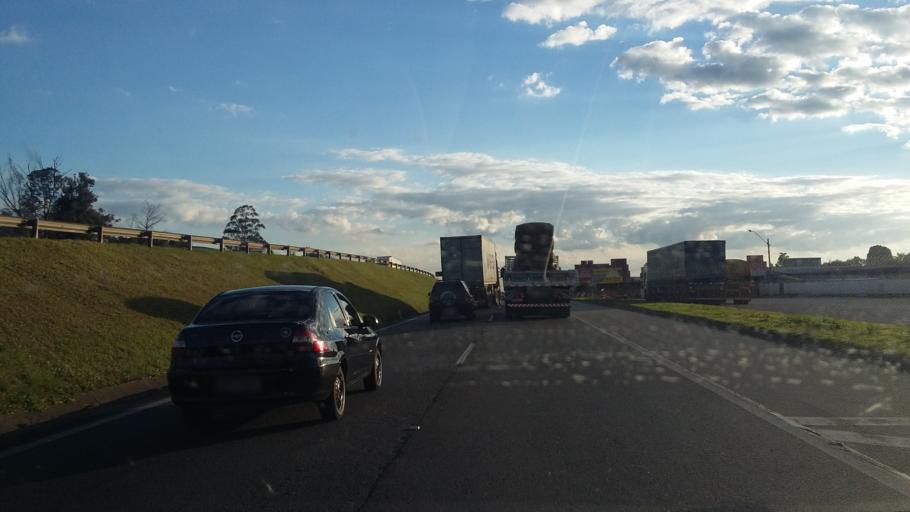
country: BR
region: Parana
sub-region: Campo Largo
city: Campo Largo
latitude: -25.4335
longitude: -49.4076
